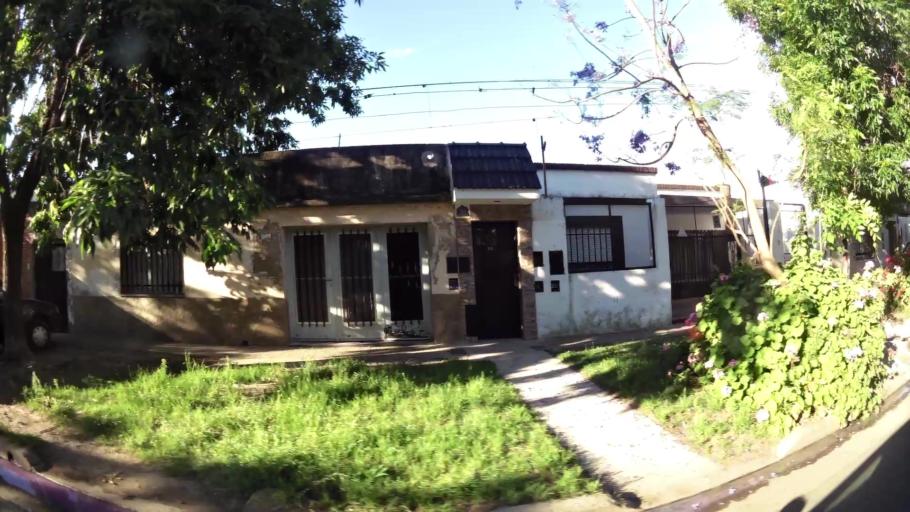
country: AR
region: Santa Fe
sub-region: Departamento de Rosario
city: Rosario
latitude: -32.9870
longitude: -60.6824
